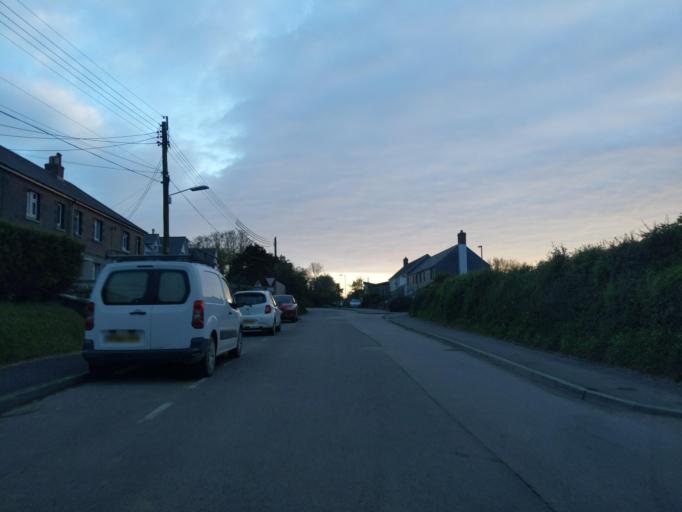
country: GB
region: England
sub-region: Cornwall
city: Polzeath
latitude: 50.5548
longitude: -4.8905
